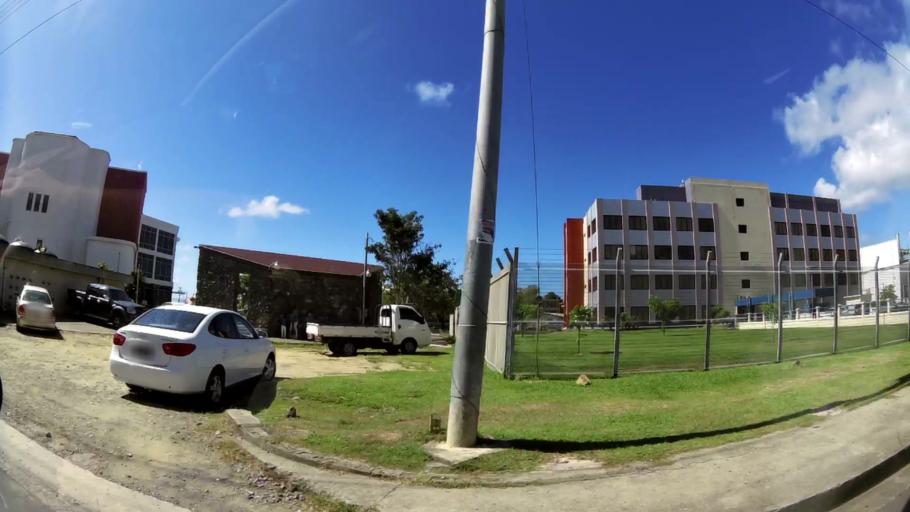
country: TT
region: Tobago
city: Scarborough
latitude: 11.1846
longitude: -60.7364
